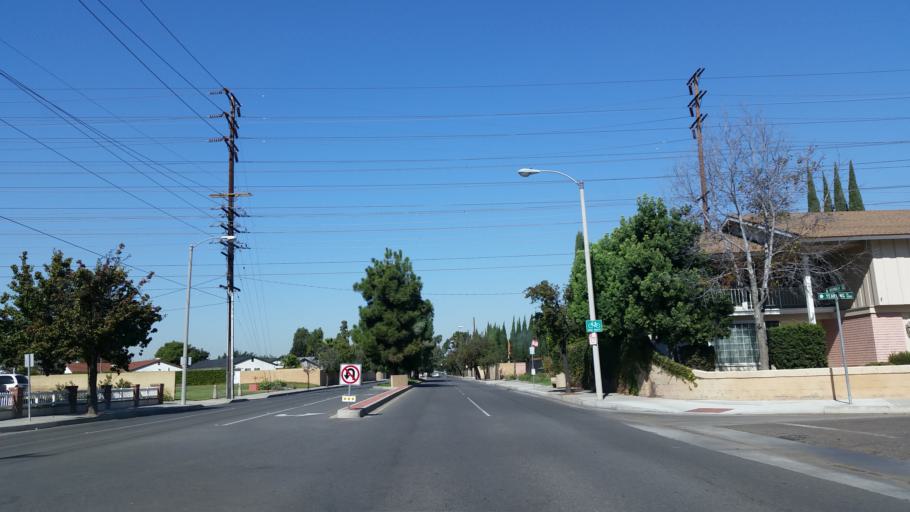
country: US
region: California
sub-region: Los Angeles County
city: Cerritos
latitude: 33.8492
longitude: -118.0721
